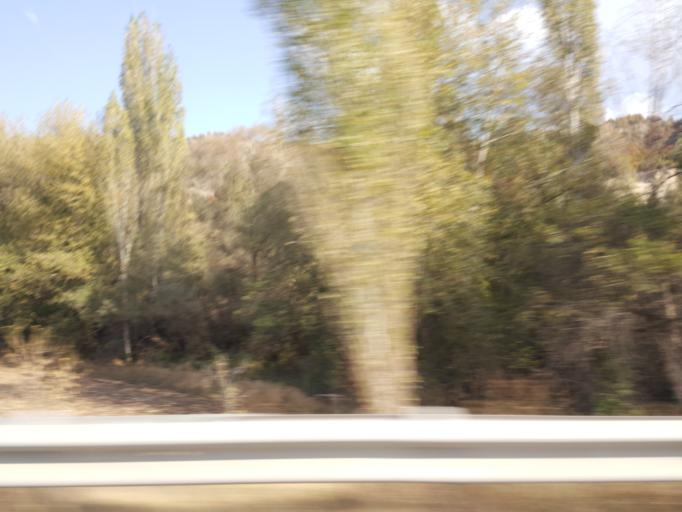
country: TR
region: Corum
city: Seydim
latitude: 40.3625
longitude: 34.7308
